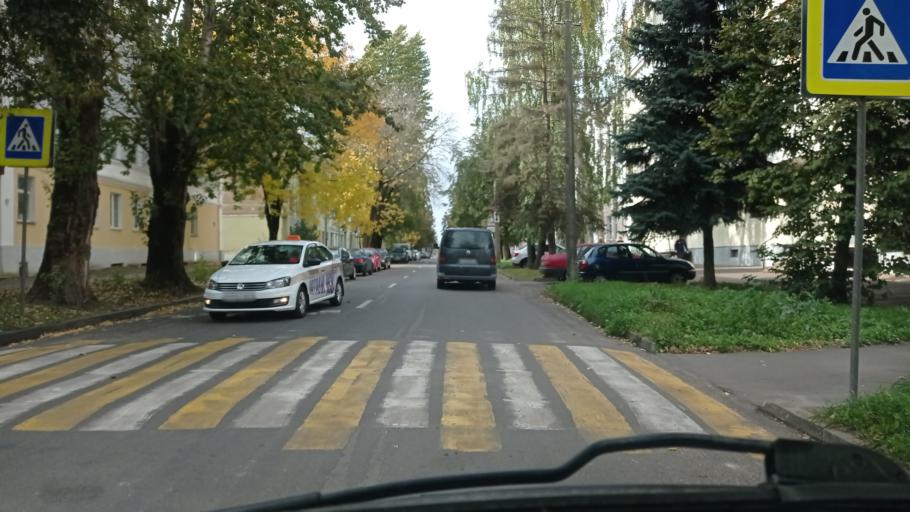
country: BY
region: Vitebsk
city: Vitebsk
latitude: 55.1832
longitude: 30.2128
